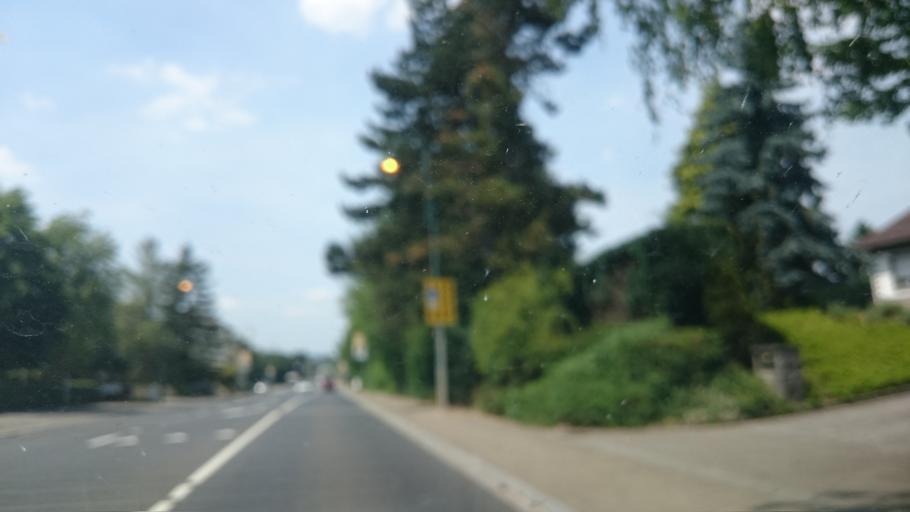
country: LU
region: Luxembourg
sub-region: Canton de Capellen
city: Mamer
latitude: 49.6328
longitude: 6.0192
